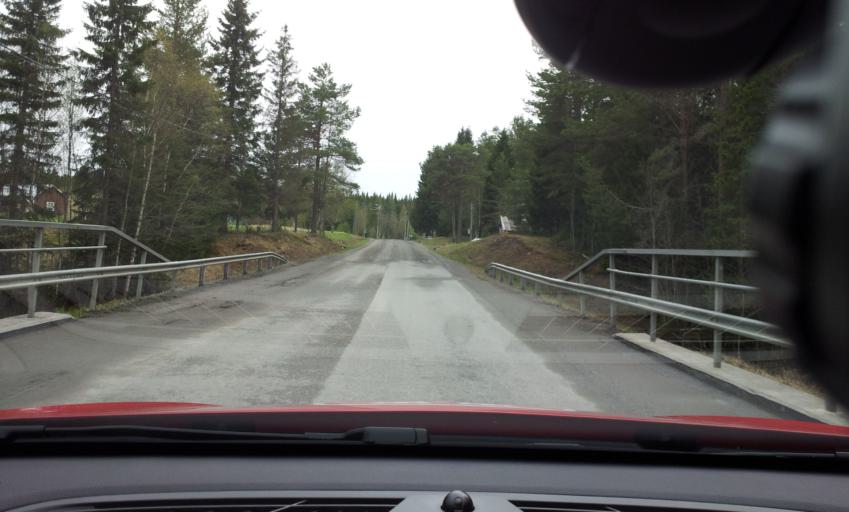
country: SE
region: Jaemtland
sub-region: OEstersunds Kommun
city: Brunflo
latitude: 63.0196
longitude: 14.7712
